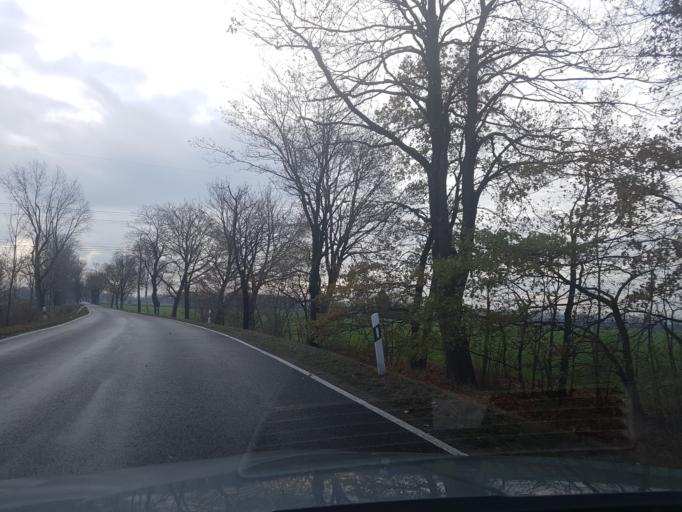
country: DE
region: Brandenburg
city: Plessa
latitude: 51.4455
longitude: 13.6202
